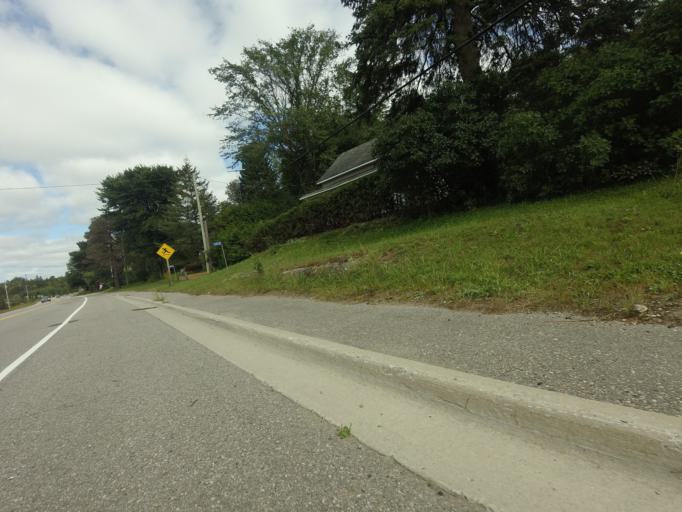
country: CA
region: Ontario
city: Bancroft
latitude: 44.9708
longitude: -78.2768
